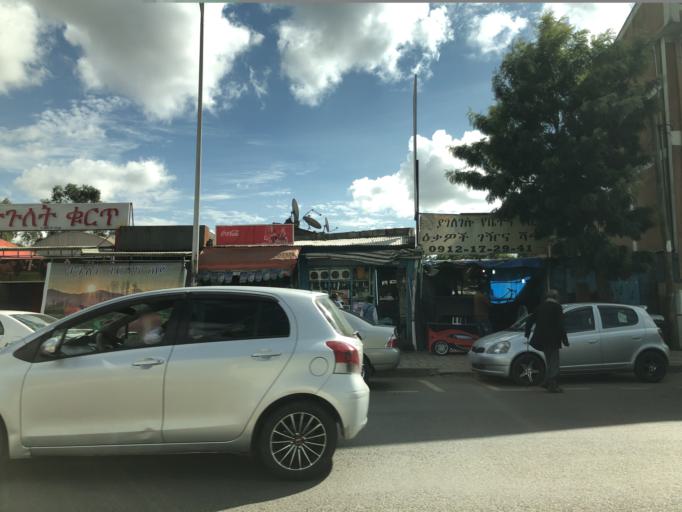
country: ET
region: Adis Abeba
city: Addis Ababa
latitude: 9.0234
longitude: 38.7794
